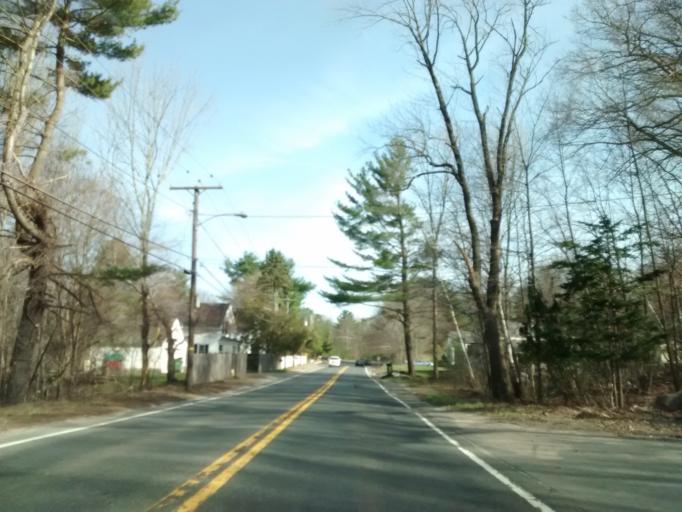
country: US
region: Massachusetts
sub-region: Worcester County
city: Whitinsville
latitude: 42.1167
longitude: -71.6397
